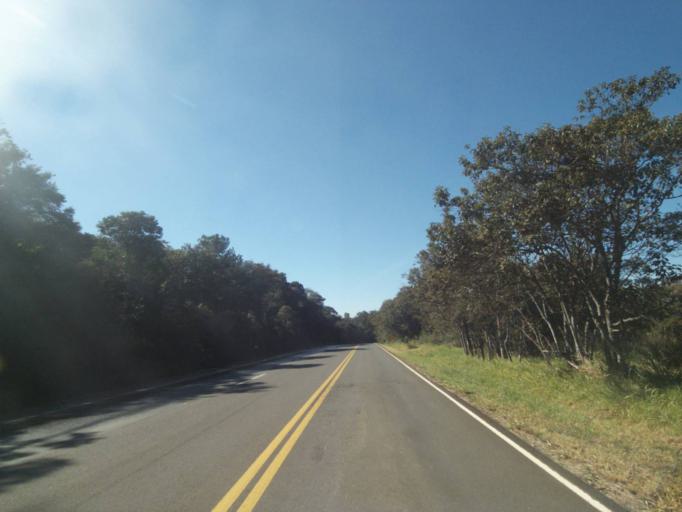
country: BR
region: Parana
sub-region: Tibagi
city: Tibagi
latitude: -24.4755
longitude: -50.5167
